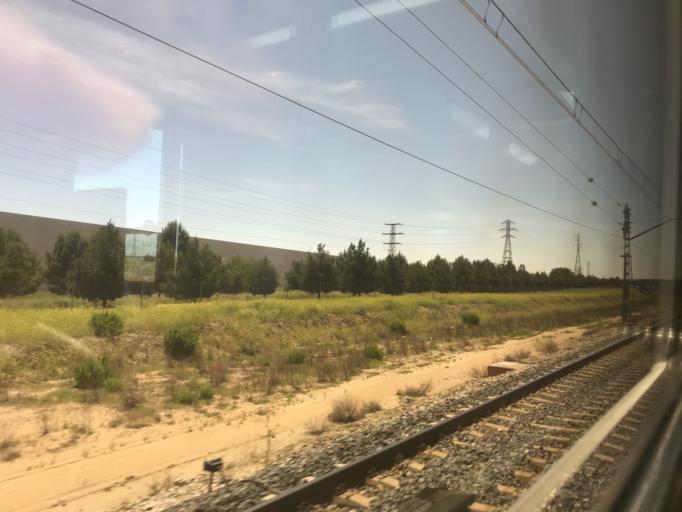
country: ES
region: Madrid
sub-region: Provincia de Madrid
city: Pinto
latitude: 40.2779
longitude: -3.7041
